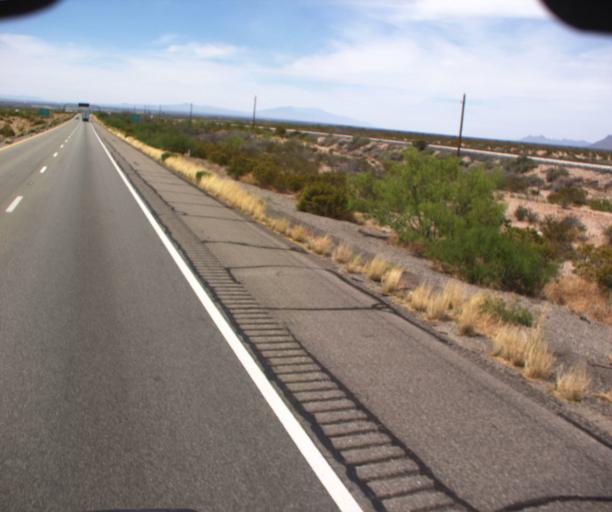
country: US
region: New Mexico
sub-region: Hidalgo County
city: Lordsburg
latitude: 32.2490
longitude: -109.1415
